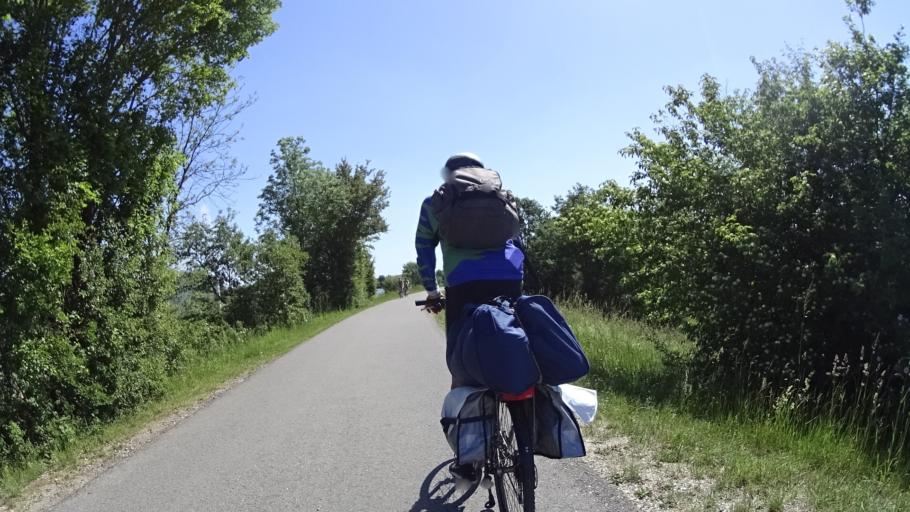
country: DE
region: Bavaria
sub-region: Regierungsbezirk Mittelfranken
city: Gunzenhausen
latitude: 49.1235
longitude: 10.7407
